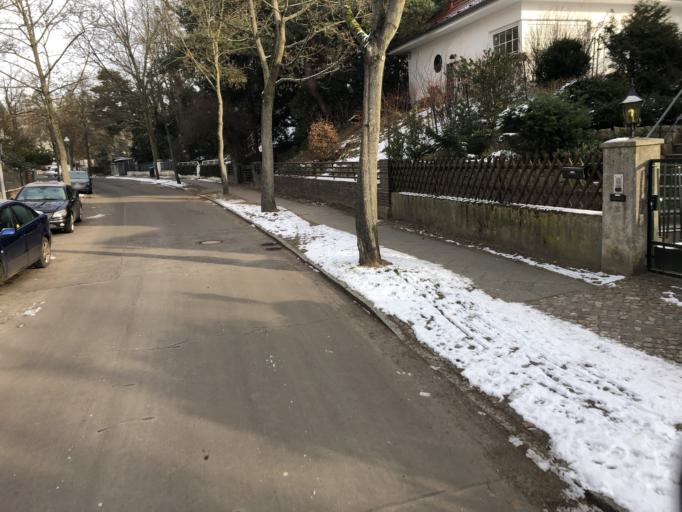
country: DE
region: Berlin
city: Frohnau
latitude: 52.6293
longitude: 13.3062
